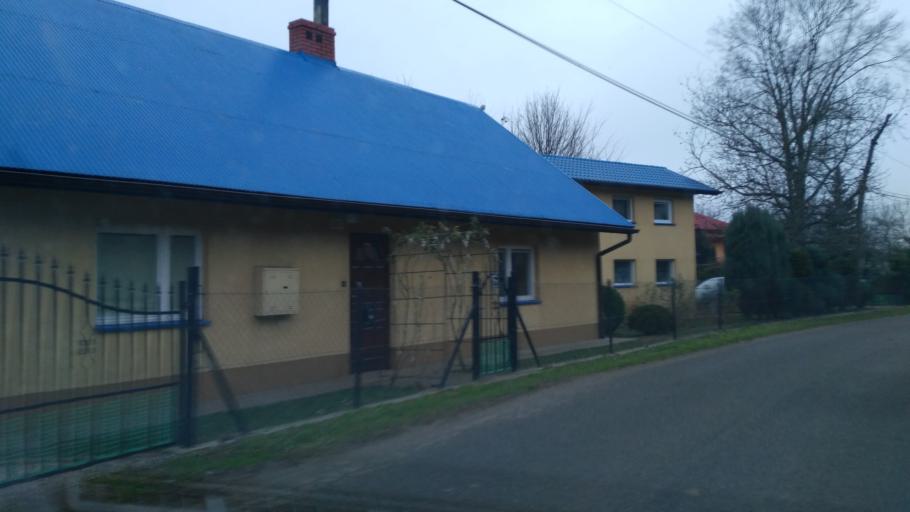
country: PL
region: Subcarpathian Voivodeship
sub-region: Powiat przeworski
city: Rozborz
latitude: 50.0526
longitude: 22.5470
